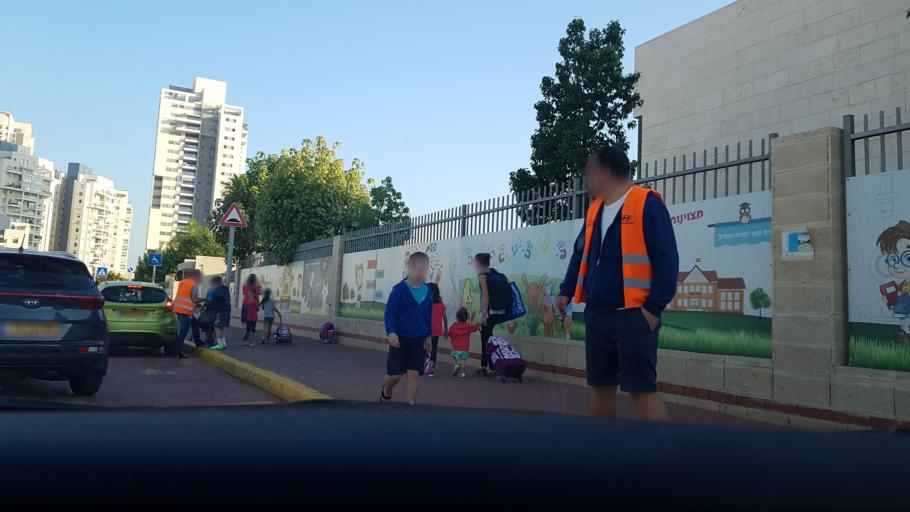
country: IL
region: Central District
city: Ness Ziona
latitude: 31.9041
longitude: 34.8238
